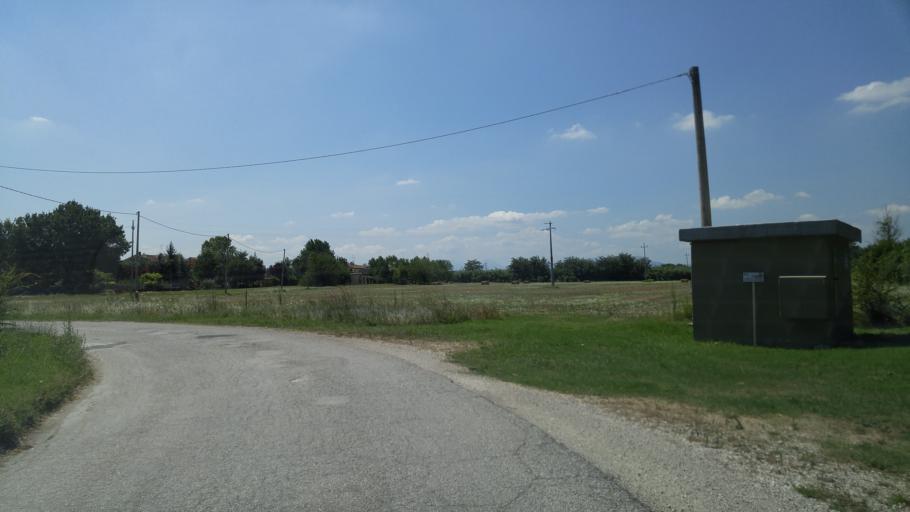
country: IT
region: The Marches
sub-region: Provincia di Pesaro e Urbino
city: Cuccurano
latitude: 43.7970
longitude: 12.9691
